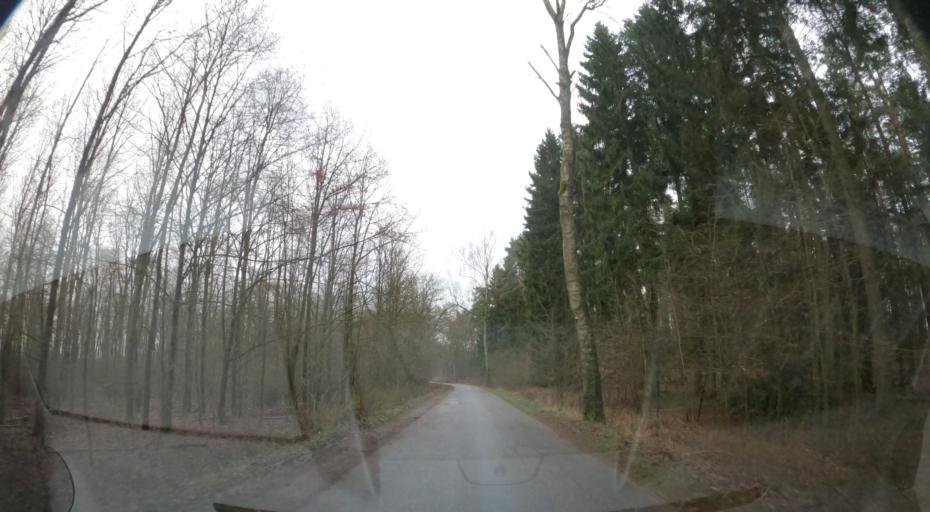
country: PL
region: Greater Poland Voivodeship
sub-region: Powiat zlotowski
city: Krajenka
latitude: 53.2827
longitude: 17.0744
